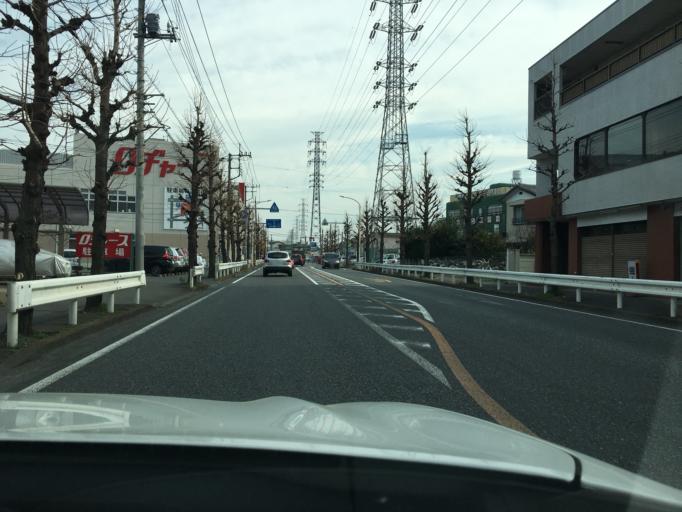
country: JP
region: Saitama
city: Kawagoe
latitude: 35.9070
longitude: 139.4726
